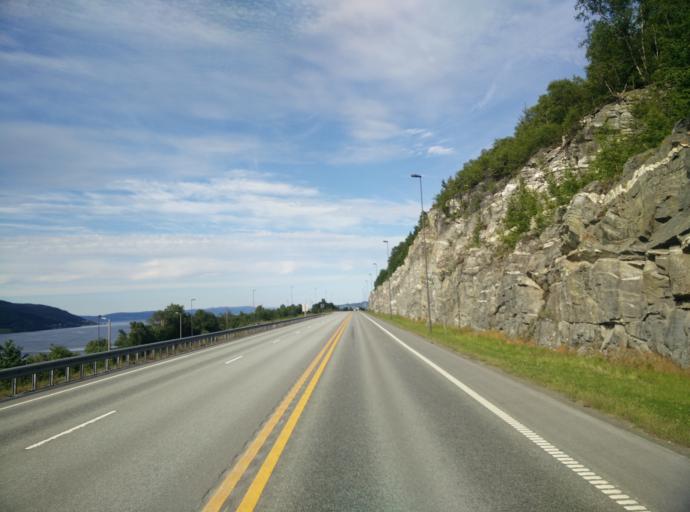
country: NO
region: Sor-Trondelag
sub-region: Orkdal
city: Orkanger
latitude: 63.3231
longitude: 9.8910
